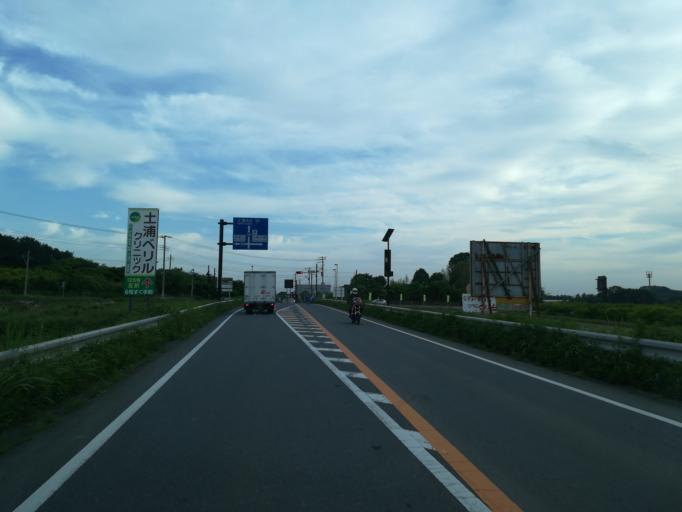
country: JP
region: Ibaraki
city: Tsukuba
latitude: 36.1595
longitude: 140.1635
